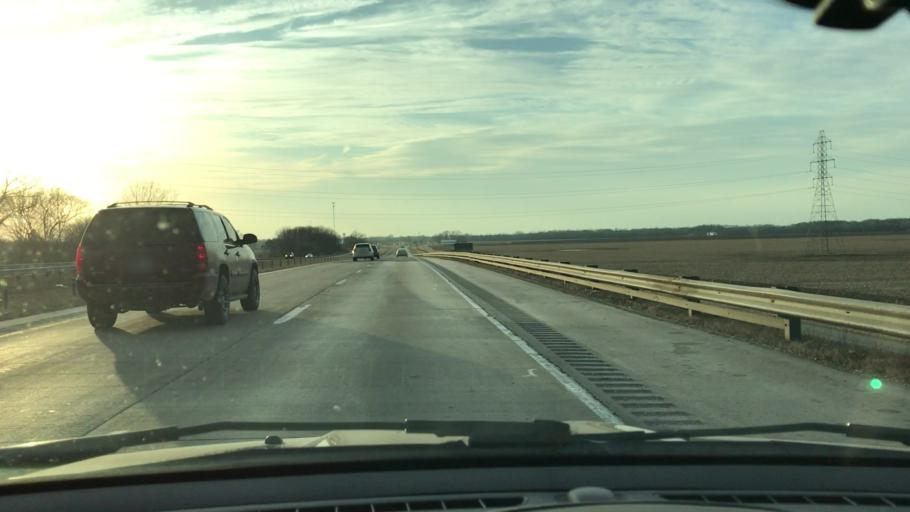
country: US
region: Indiana
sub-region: Wayne County
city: Cambridge City
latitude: 39.8539
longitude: -85.1059
